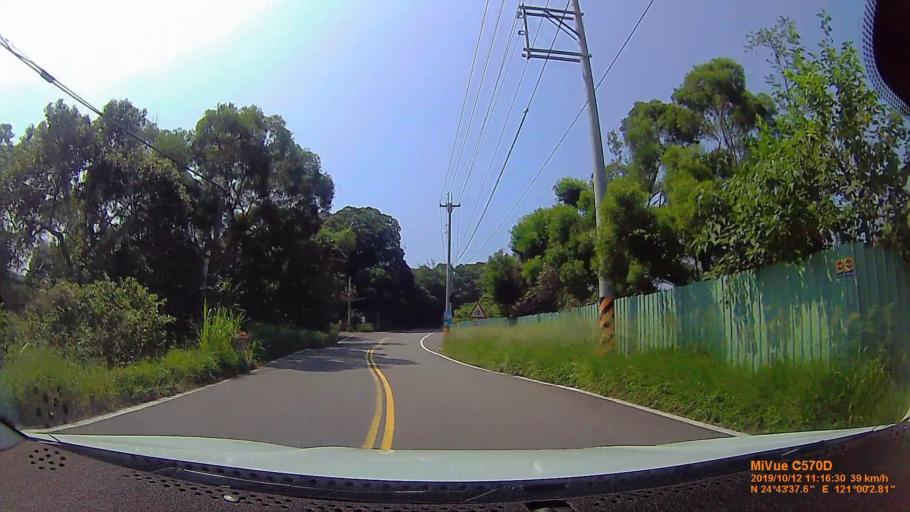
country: TW
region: Taiwan
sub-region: Hsinchu
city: Hsinchu
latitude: 24.7270
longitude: 121.0007
